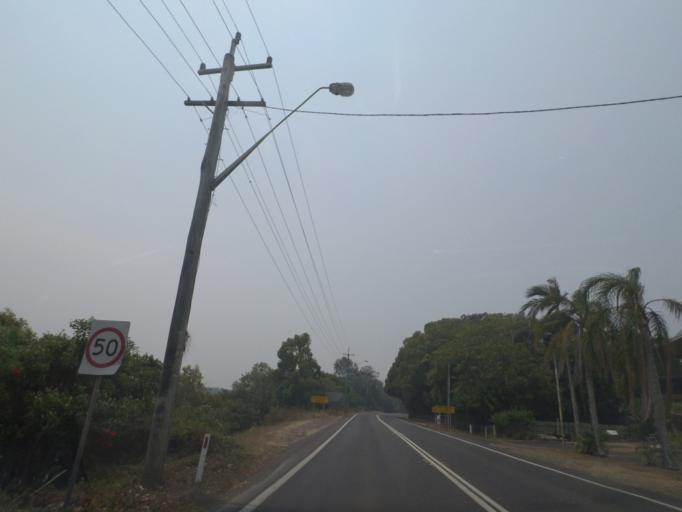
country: AU
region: New South Wales
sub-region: Richmond Valley
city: Evans Head
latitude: -29.0035
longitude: 153.4366
